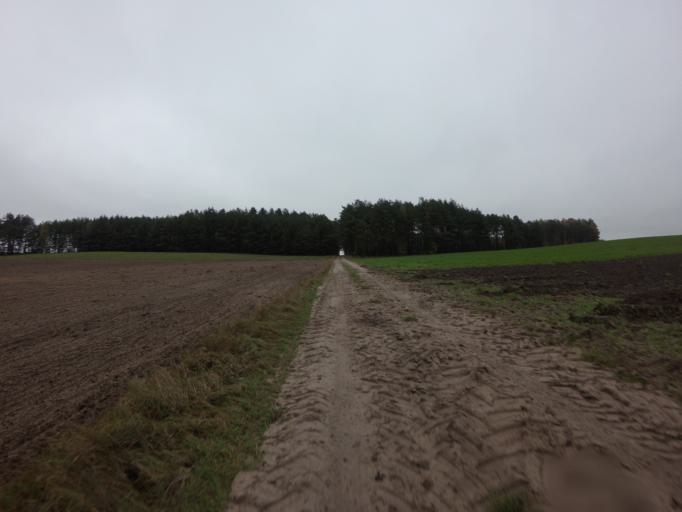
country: PL
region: Pomeranian Voivodeship
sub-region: Powiat kartuski
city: Stezyca
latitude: 54.1712
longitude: 17.9372
